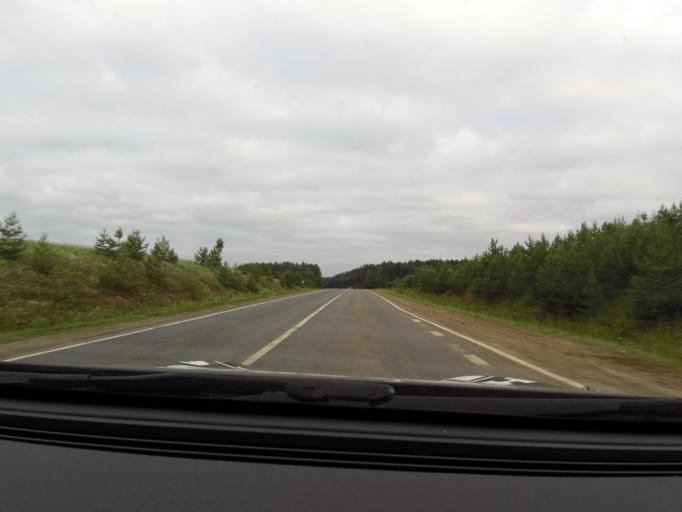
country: RU
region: Perm
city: Siva
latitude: 58.4115
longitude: 54.4697
